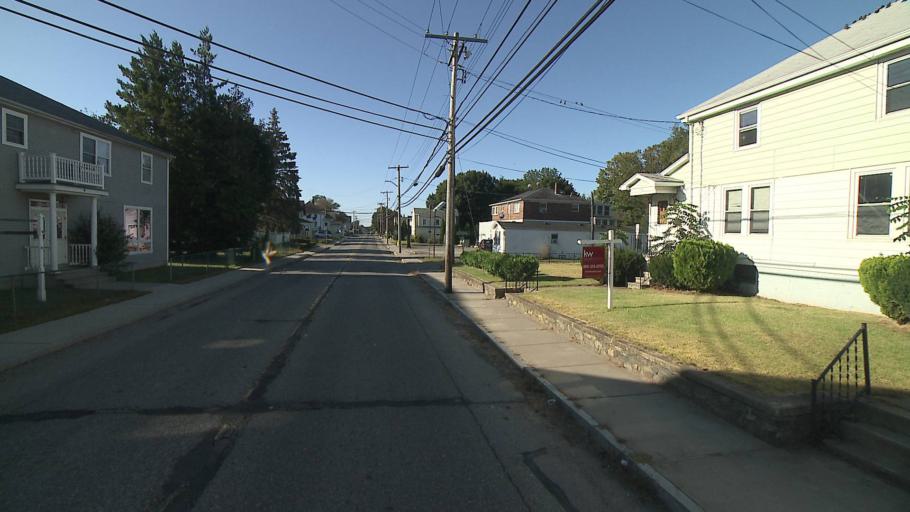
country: US
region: Connecticut
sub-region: New London County
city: Jewett City
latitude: 41.6137
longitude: -71.9794
